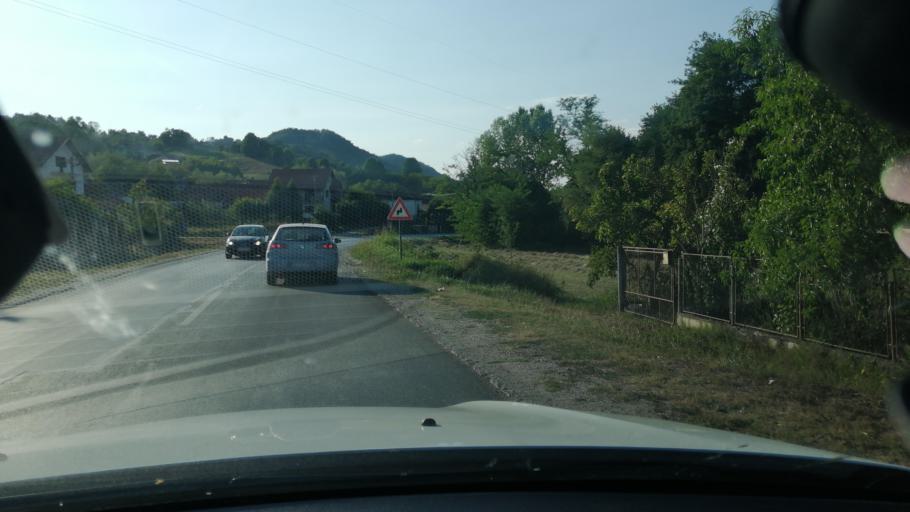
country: RS
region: Central Serbia
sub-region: Moravicki Okrug
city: Lucani
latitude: 43.7564
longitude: 20.2519
